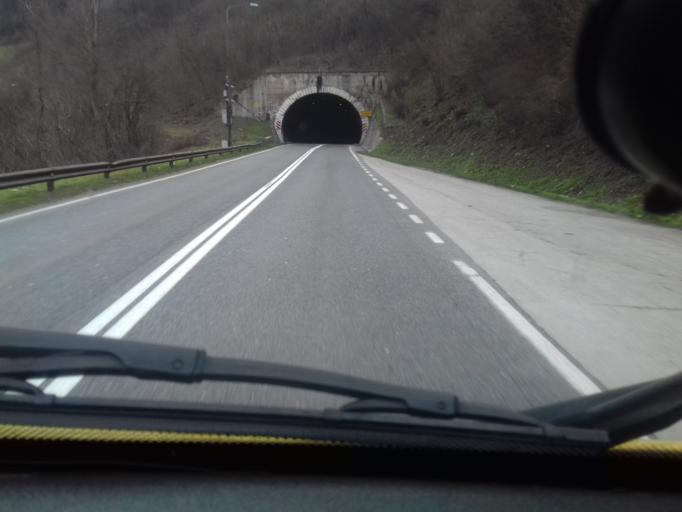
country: BA
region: Federation of Bosnia and Herzegovina
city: Zenica
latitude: 44.3017
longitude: 17.9086
